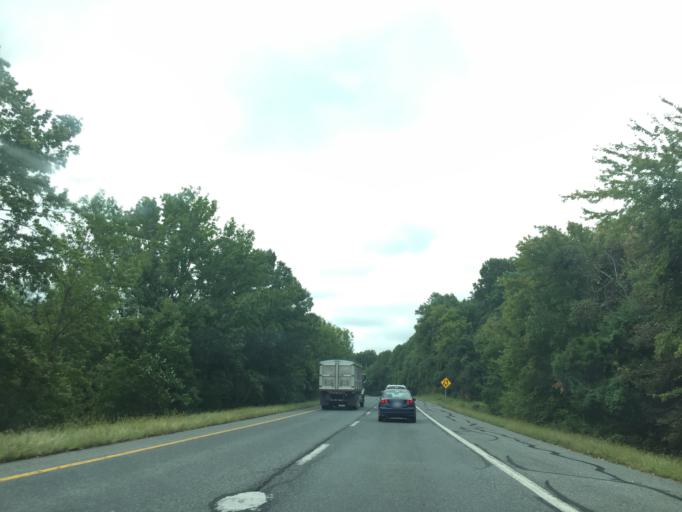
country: US
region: Maryland
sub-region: Harford County
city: Fallston
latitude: 39.5131
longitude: -76.3788
